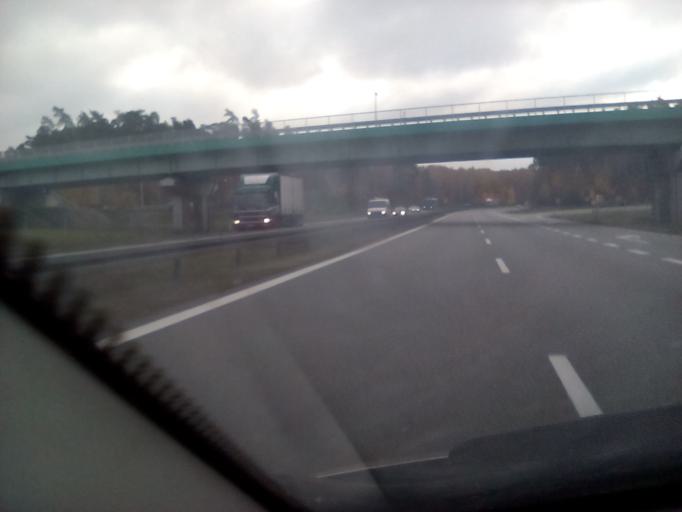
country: PL
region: Masovian Voivodeship
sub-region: Powiat bialobrzeski
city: Bialobrzegi
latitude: 51.6500
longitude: 20.9716
